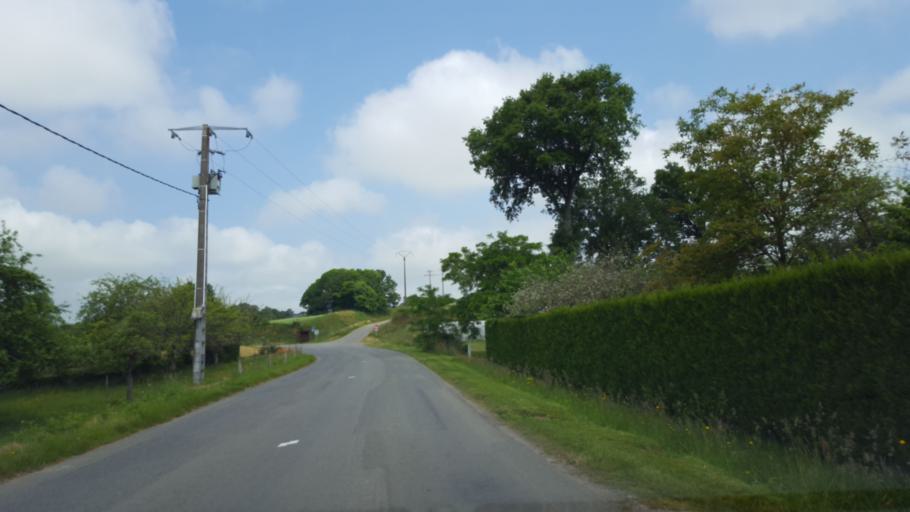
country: FR
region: Brittany
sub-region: Departement d'Ille-et-Vilaine
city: Baulon
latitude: 47.9261
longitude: -1.9232
